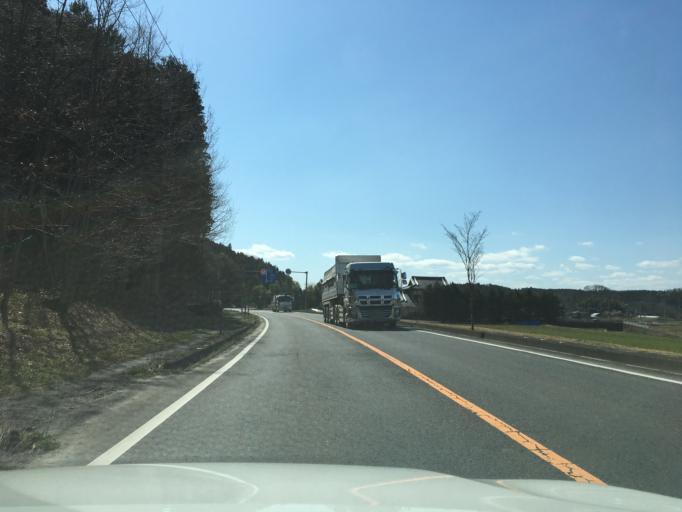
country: JP
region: Tochigi
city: Kuroiso
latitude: 36.9462
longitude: 140.1460
